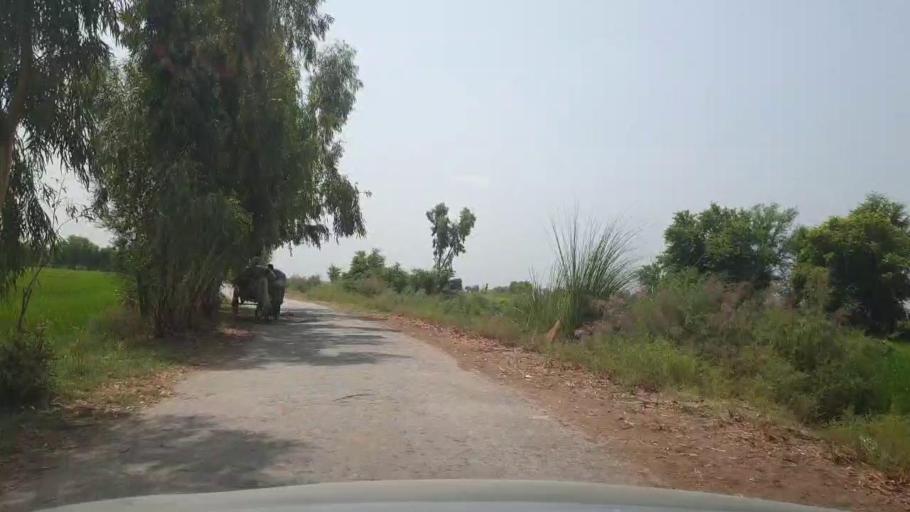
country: PK
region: Sindh
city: Garhi Yasin
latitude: 27.9442
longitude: 68.3756
